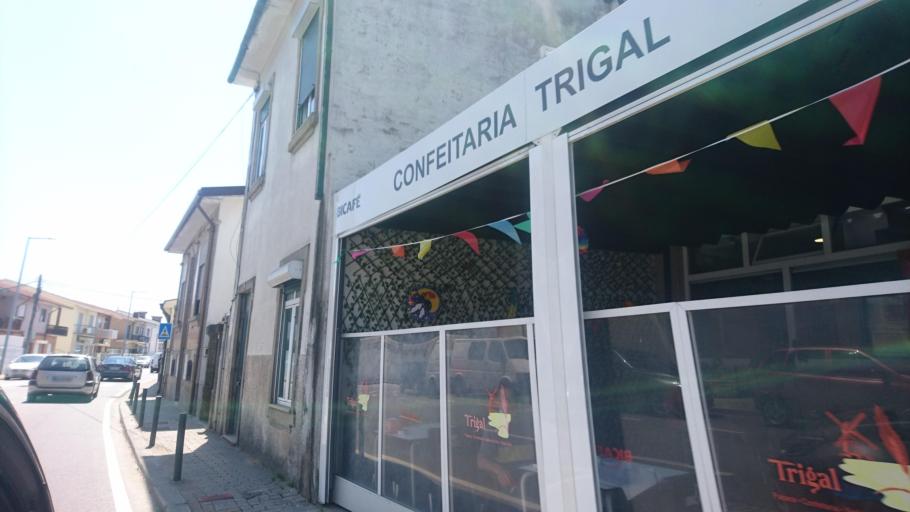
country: PT
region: Porto
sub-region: Gondomar
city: Rio Tinto
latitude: 41.1652
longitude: -8.5468
